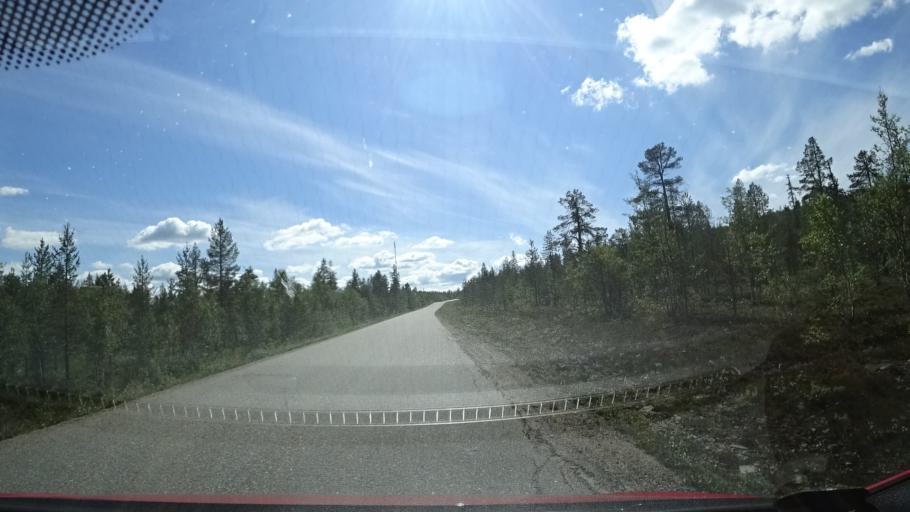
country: FI
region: Lapland
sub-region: Pohjois-Lappi
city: Inari
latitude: 68.5908
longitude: 26.2466
